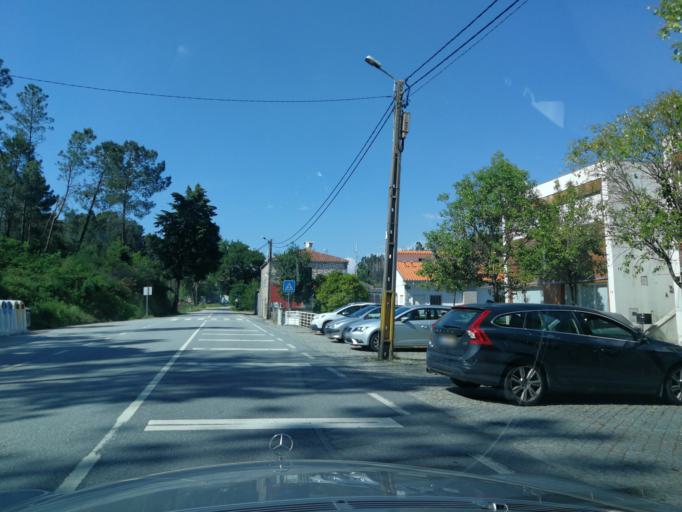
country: PT
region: Braga
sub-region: Braga
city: Adaufe
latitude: 41.5788
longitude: -8.3712
